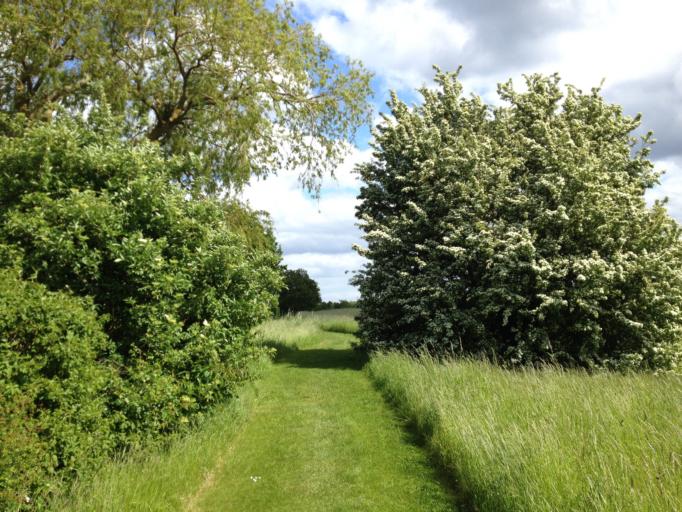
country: DK
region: Capital Region
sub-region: Fredensborg Kommune
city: Niva
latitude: 55.9319
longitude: 12.4877
